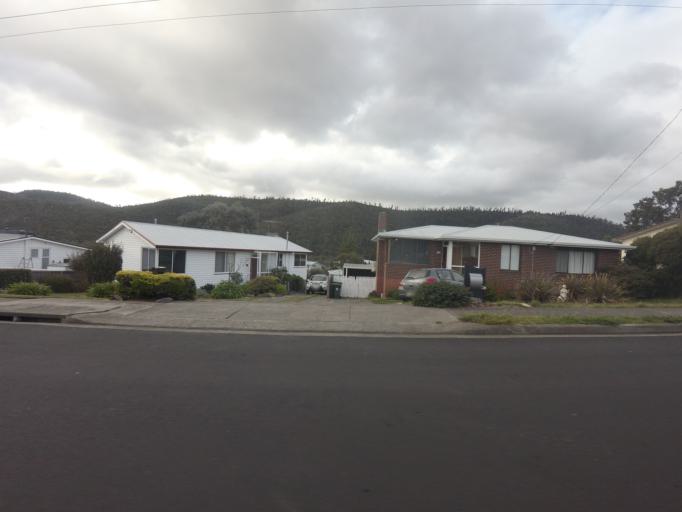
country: AU
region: Tasmania
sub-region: Clarence
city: Warrane
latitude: -42.8576
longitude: 147.3979
